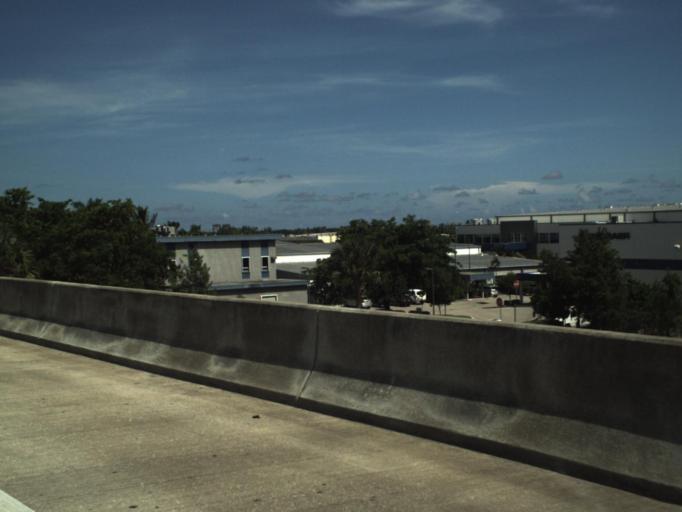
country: US
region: Florida
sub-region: Broward County
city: Dania Beach
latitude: 26.0813
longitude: -80.1453
